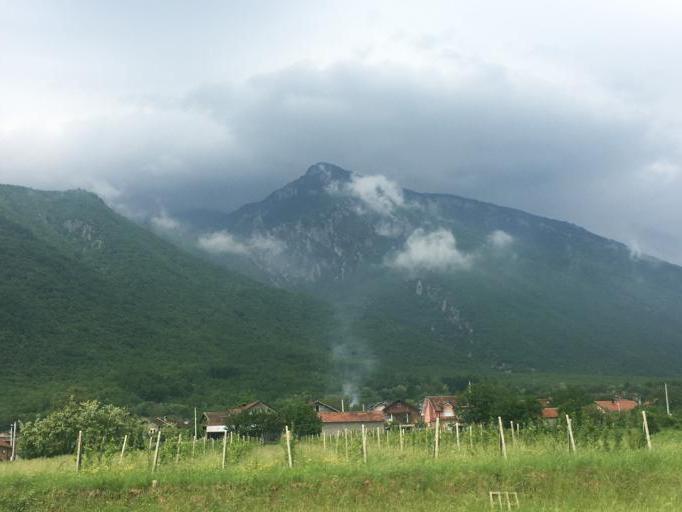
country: XK
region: Gjakova
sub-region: Komuna e Decanit
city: Strellc i Eperm
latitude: 42.5962
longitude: 20.2957
